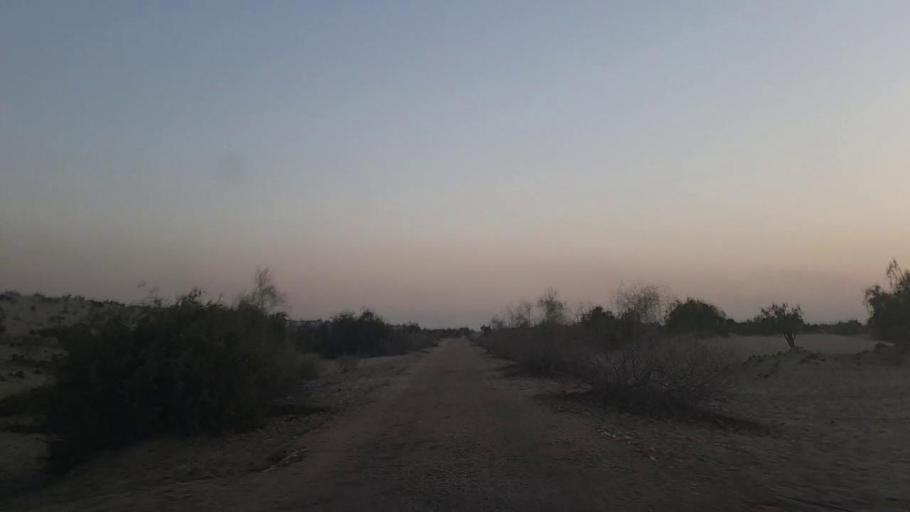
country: PK
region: Sindh
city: Jam Sahib
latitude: 26.4002
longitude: 68.8096
